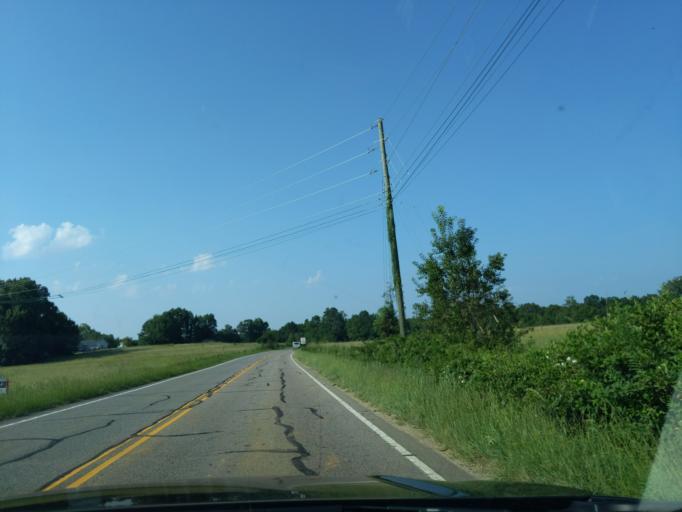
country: US
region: South Carolina
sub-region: Newberry County
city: Prosperity
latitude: 34.1307
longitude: -81.5416
